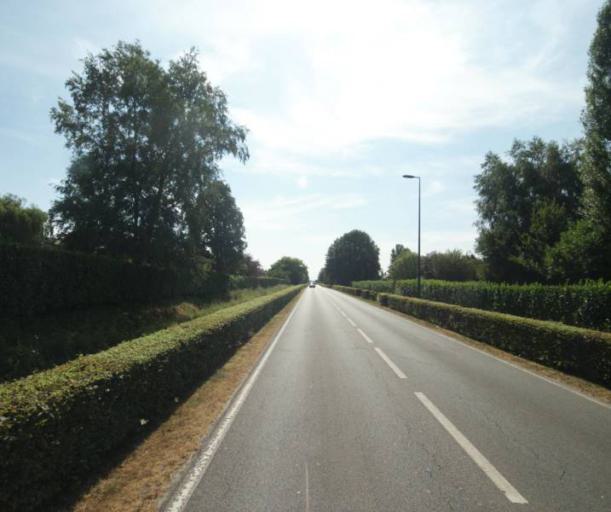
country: FR
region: Nord-Pas-de-Calais
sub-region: Departement du Nord
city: Bondues
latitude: 50.7058
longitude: 3.0894
